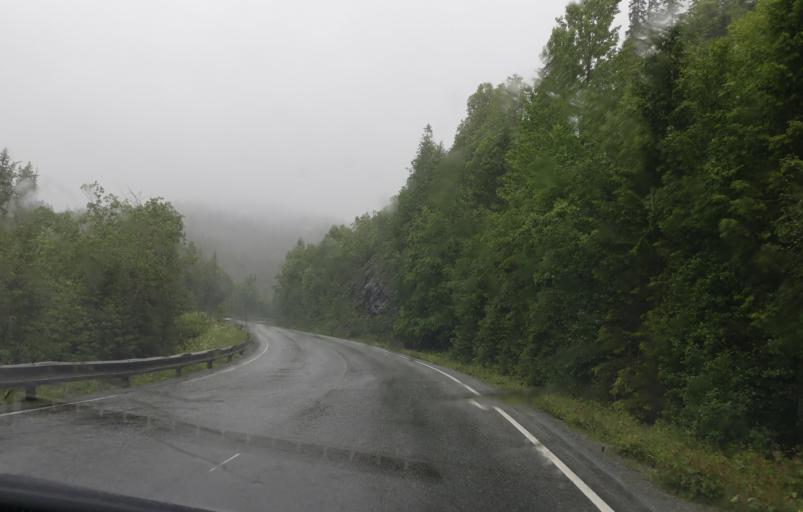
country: NO
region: Sor-Trondelag
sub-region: Selbu
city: Mebonden
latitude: 63.3634
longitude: 11.0752
